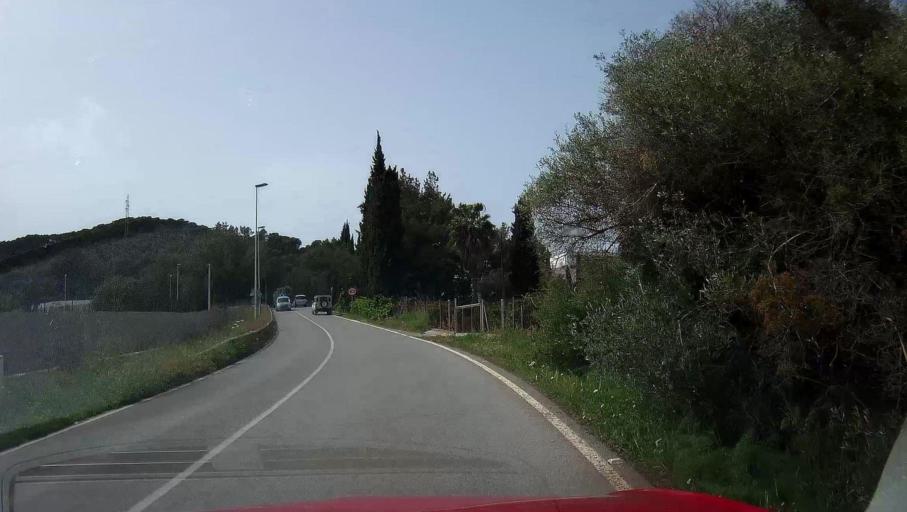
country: ES
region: Balearic Islands
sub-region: Illes Balears
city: Santa Eularia des Riu
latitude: 38.9906
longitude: 1.4864
